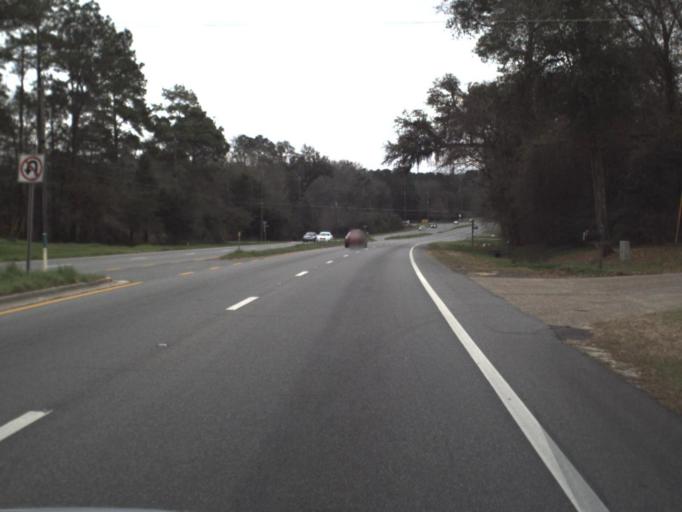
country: US
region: Florida
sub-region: Leon County
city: Tallahassee
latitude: 30.4292
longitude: -84.1976
